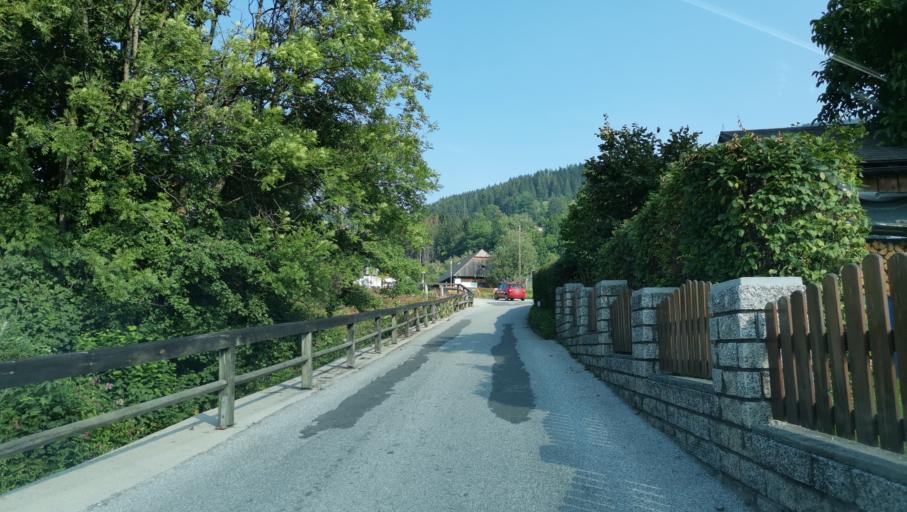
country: AT
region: Styria
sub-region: Politischer Bezirk Liezen
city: Trieben
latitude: 47.5025
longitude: 14.4772
